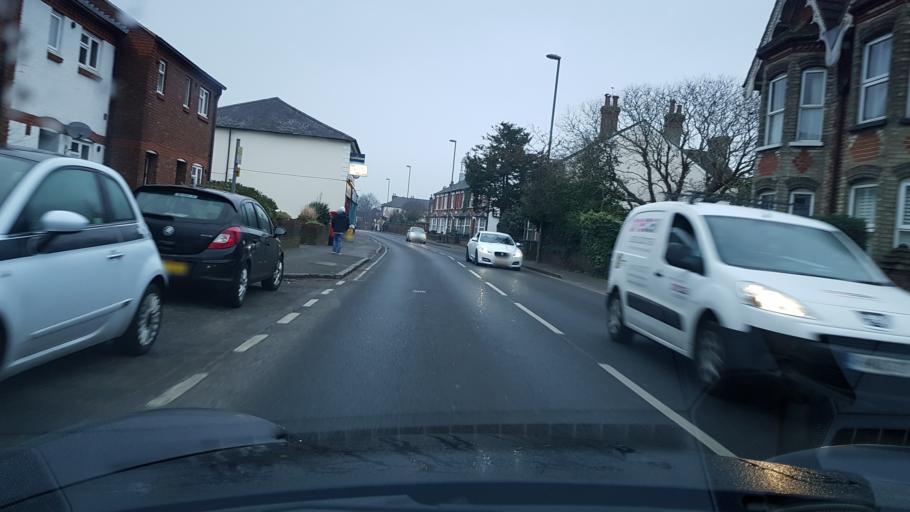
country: GB
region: England
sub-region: Surrey
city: Guildford
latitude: 51.2407
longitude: -0.5713
